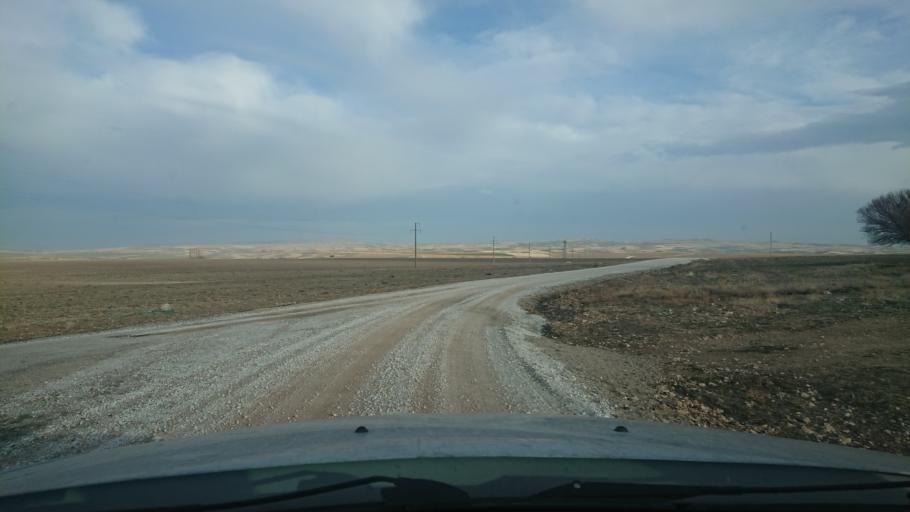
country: TR
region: Aksaray
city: Agacoren
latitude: 38.7216
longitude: 33.8666
